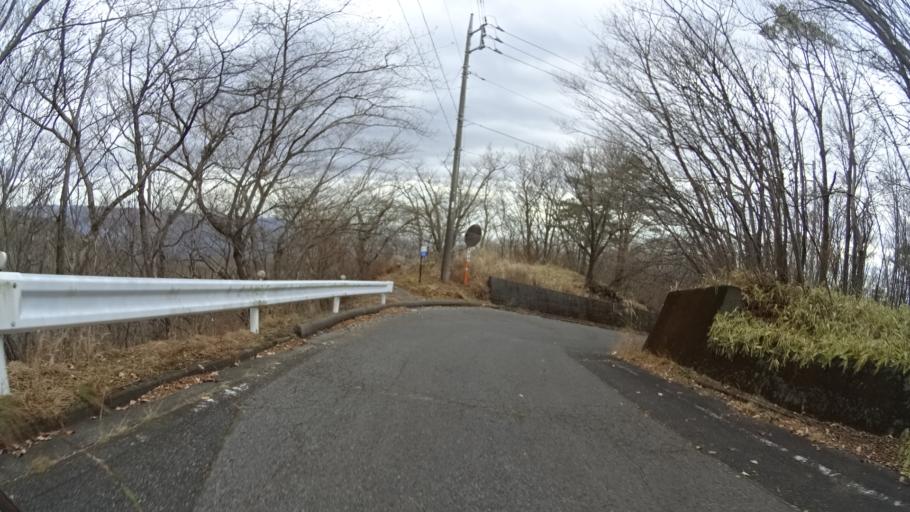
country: JP
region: Gunma
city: Omamacho-omama
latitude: 36.5124
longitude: 139.1842
